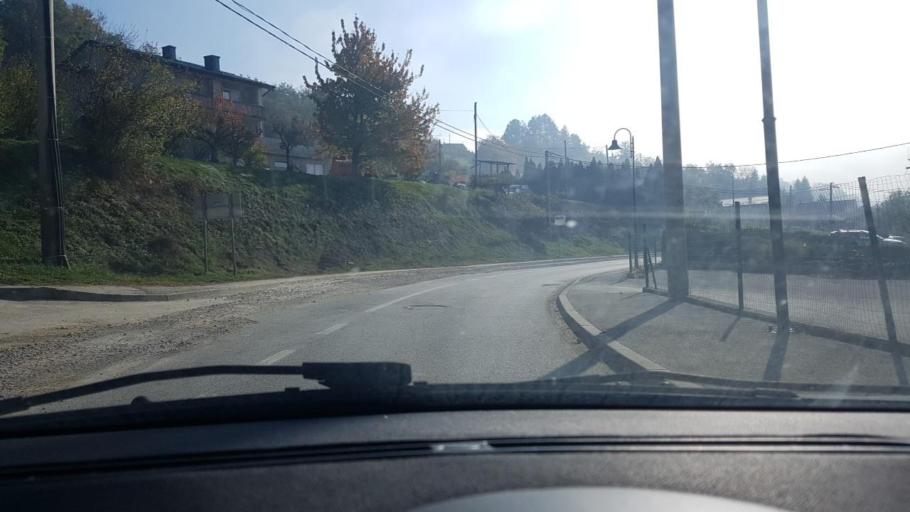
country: HR
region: Krapinsko-Zagorska
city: Zlatar
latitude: 46.1489
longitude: 16.0667
